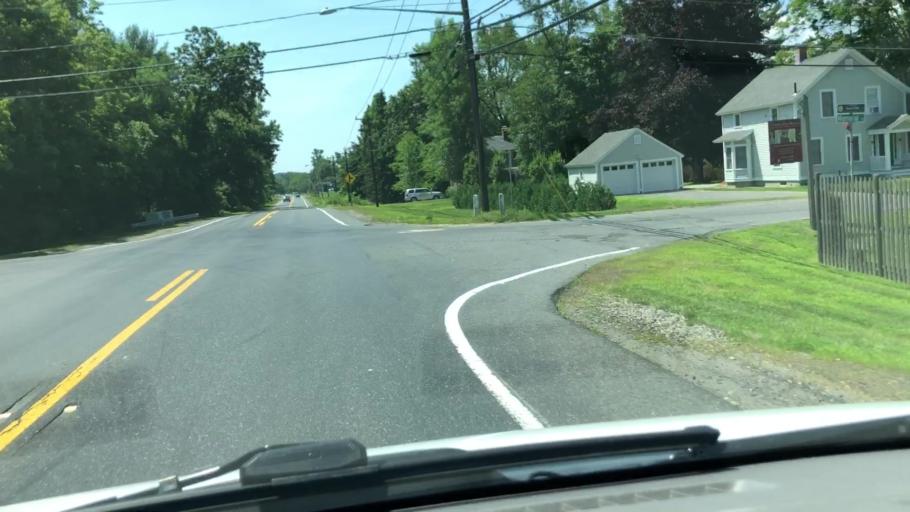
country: US
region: Massachusetts
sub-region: Franklin County
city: Greenfield
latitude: 42.5433
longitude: -72.6018
